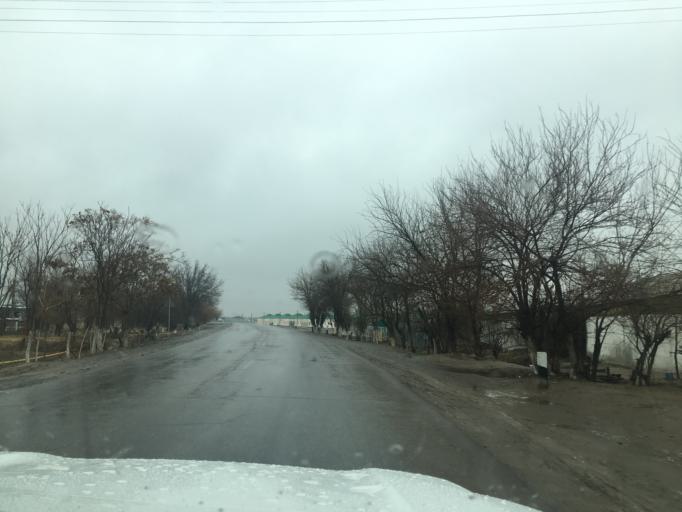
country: TM
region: Mary
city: Yoloeten
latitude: 37.2951
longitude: 62.3335
